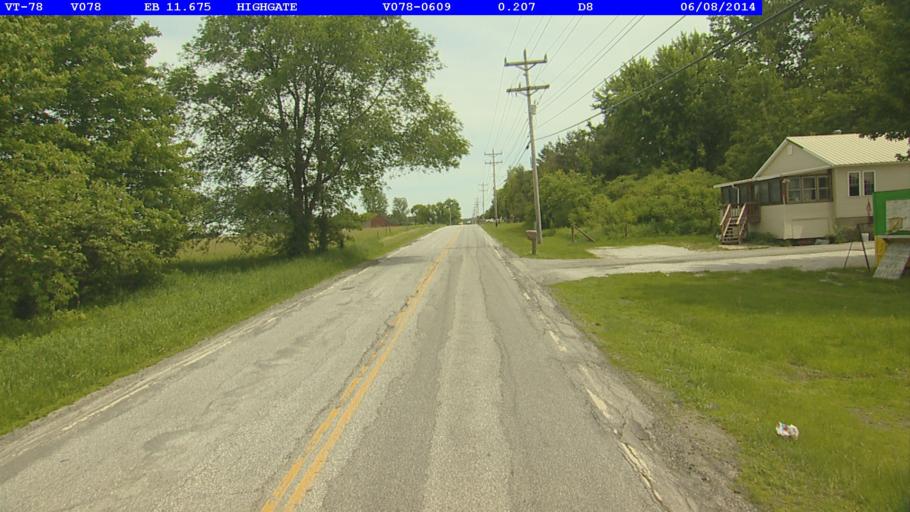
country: US
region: Vermont
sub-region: Franklin County
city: Swanton
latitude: 44.9275
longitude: -73.0949
